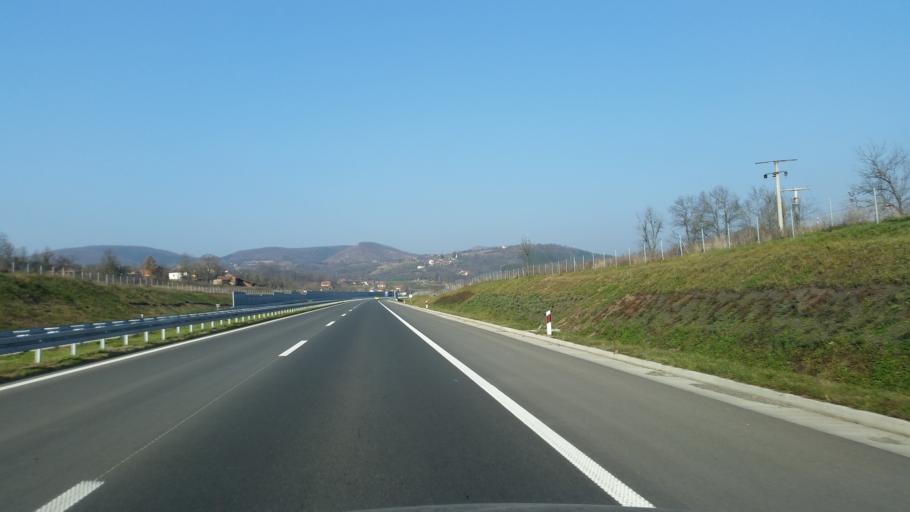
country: RS
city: Prislonica
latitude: 43.9583
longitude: 20.3982
